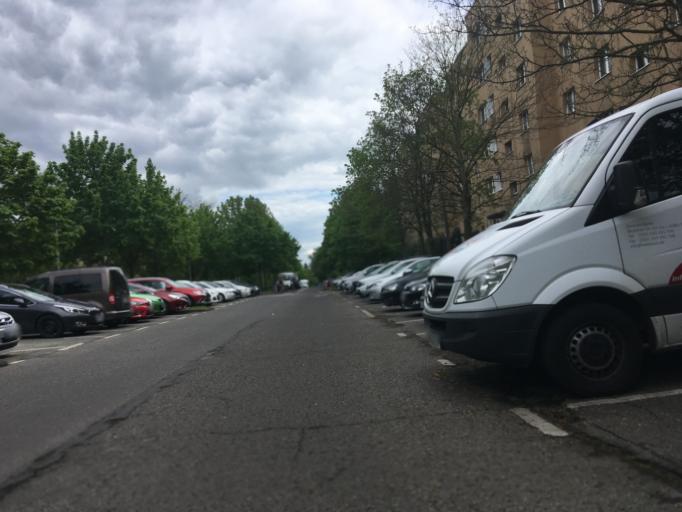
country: DE
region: Berlin
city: Marzahn
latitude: 52.5547
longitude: 13.5769
